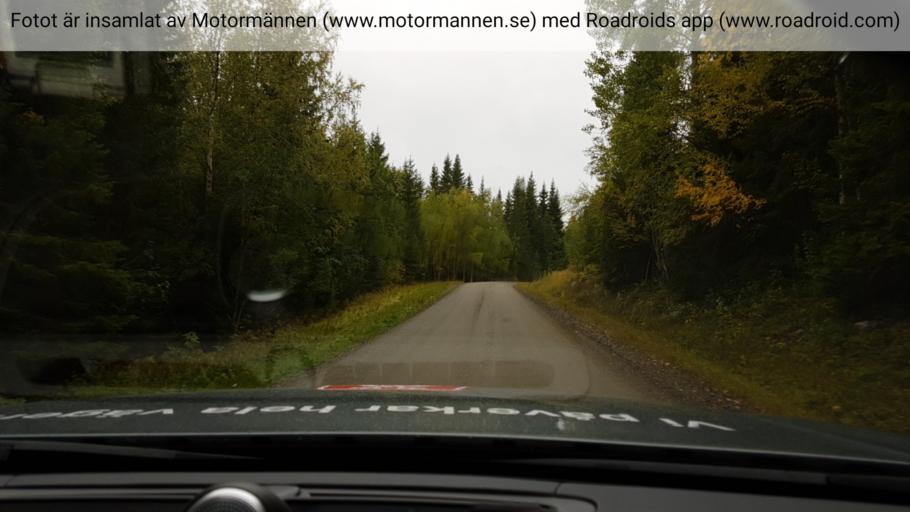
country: NO
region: Nord-Trondelag
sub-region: Lierne
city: Sandvika
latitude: 64.4627
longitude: 14.2693
